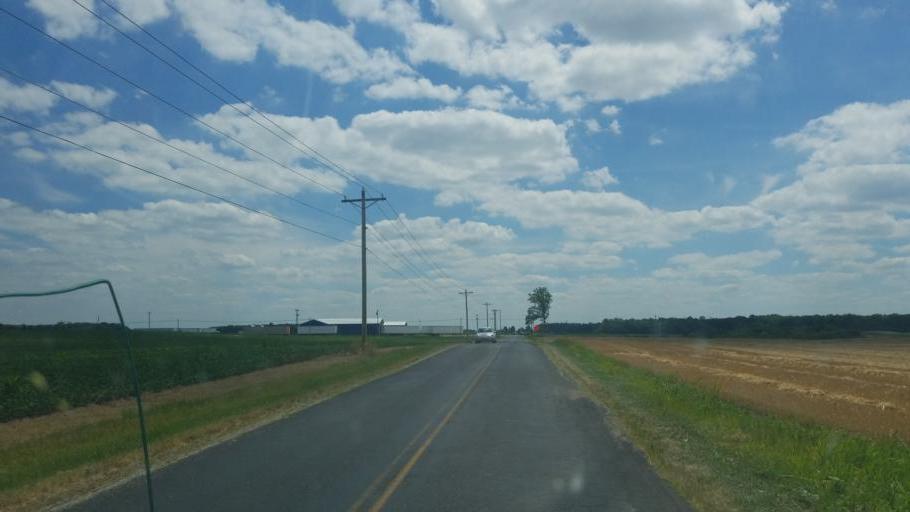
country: US
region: Ohio
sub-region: Williams County
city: Edgerton
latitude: 41.4511
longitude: -84.6911
